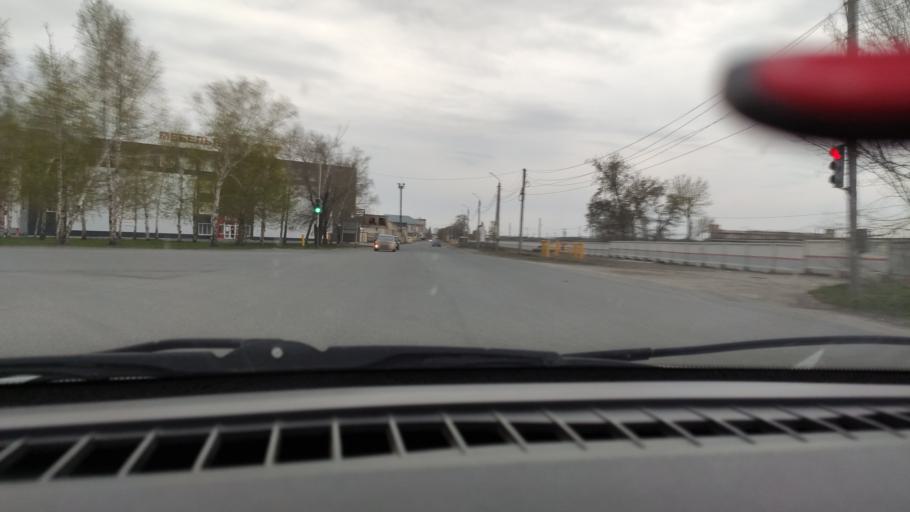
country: RU
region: Orenburg
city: Orenburg
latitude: 51.8294
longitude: 55.1078
